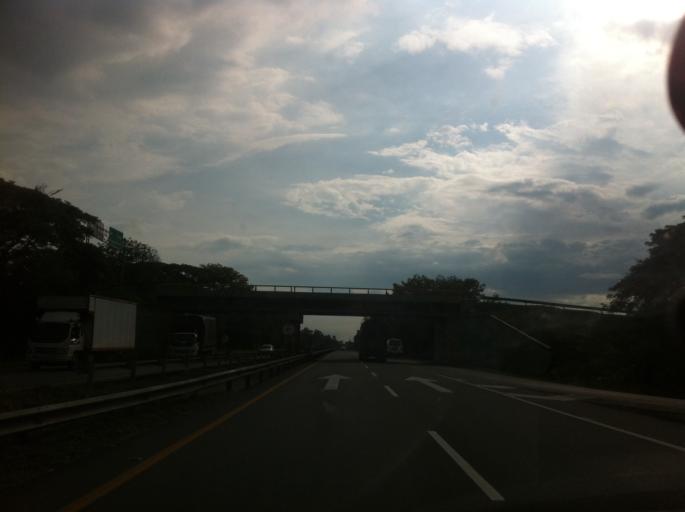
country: CO
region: Valle del Cauca
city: San Pedro
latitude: 3.9662
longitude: -76.2596
